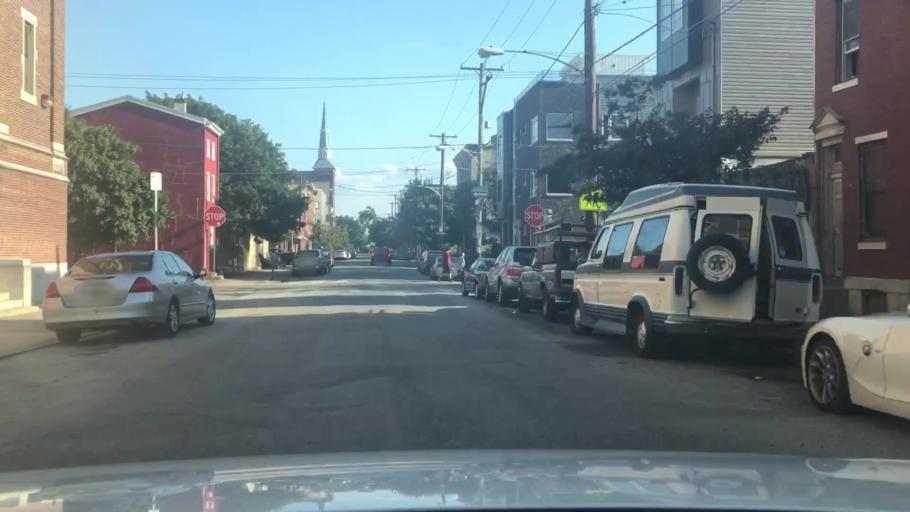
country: US
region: Pennsylvania
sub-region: Philadelphia County
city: Philadelphia
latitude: 39.9840
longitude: -75.1265
